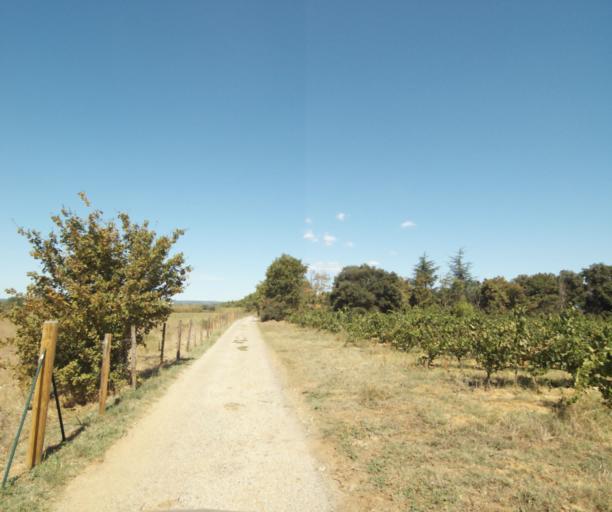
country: FR
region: Languedoc-Roussillon
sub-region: Departement du Gard
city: Bouillargues
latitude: 43.8116
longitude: 4.4226
